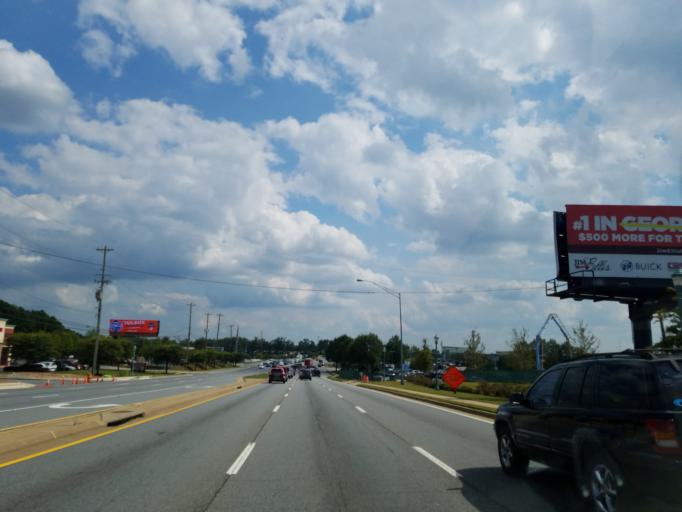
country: US
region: Georgia
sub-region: Gwinnett County
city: Buford
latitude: 34.0805
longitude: -83.9866
